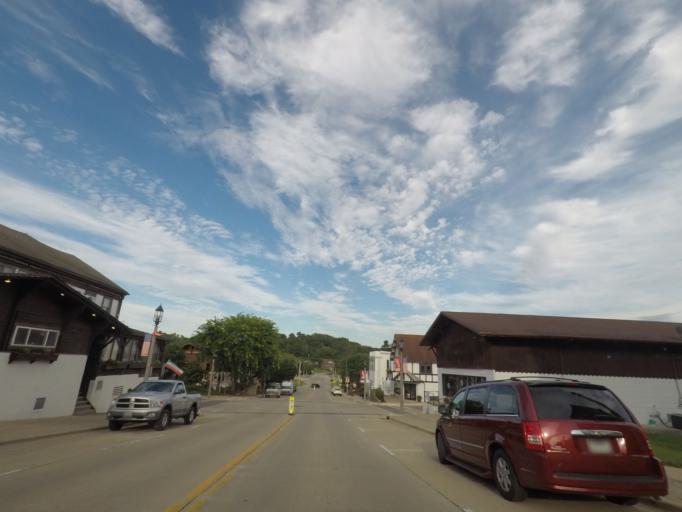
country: US
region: Wisconsin
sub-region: Green County
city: New Glarus
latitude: 42.8147
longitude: -89.6342
